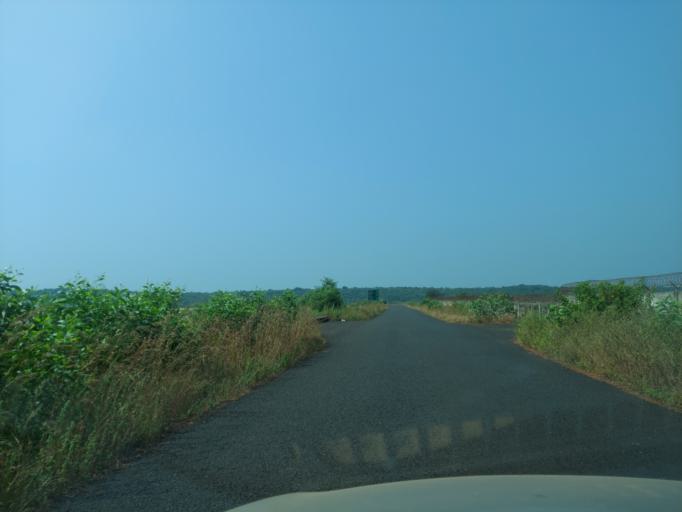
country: IN
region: Maharashtra
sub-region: Sindhudurg
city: Malvan
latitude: 15.9984
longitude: 73.5105
